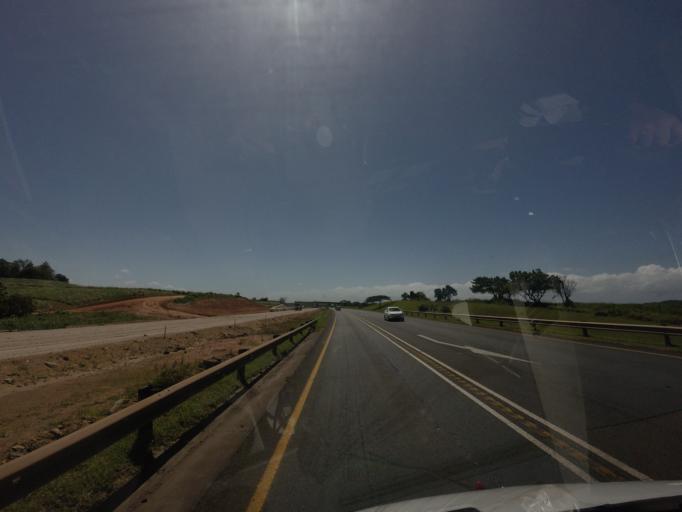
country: ZA
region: KwaZulu-Natal
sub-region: uThungulu District Municipality
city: eSikhawini
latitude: -28.9306
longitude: 31.7823
